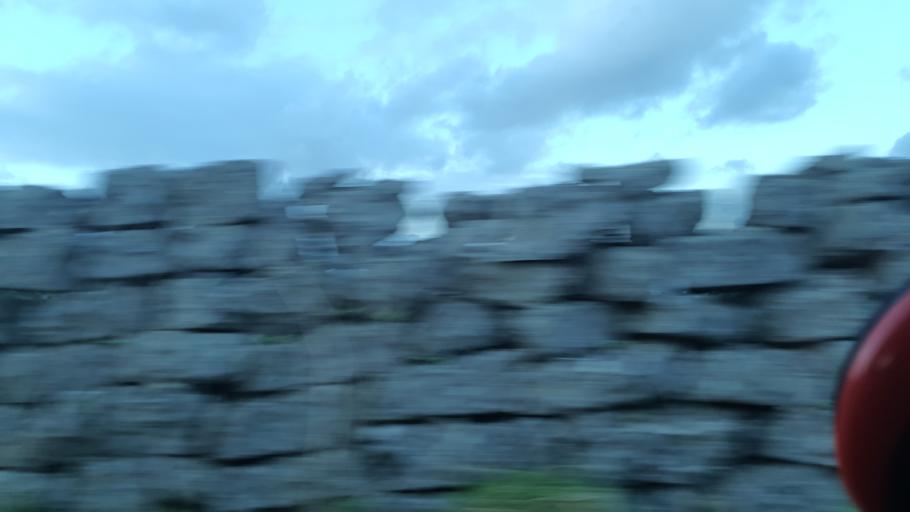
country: GB
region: Northern Ireland
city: Kilkeel
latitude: 54.0393
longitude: -6.0874
